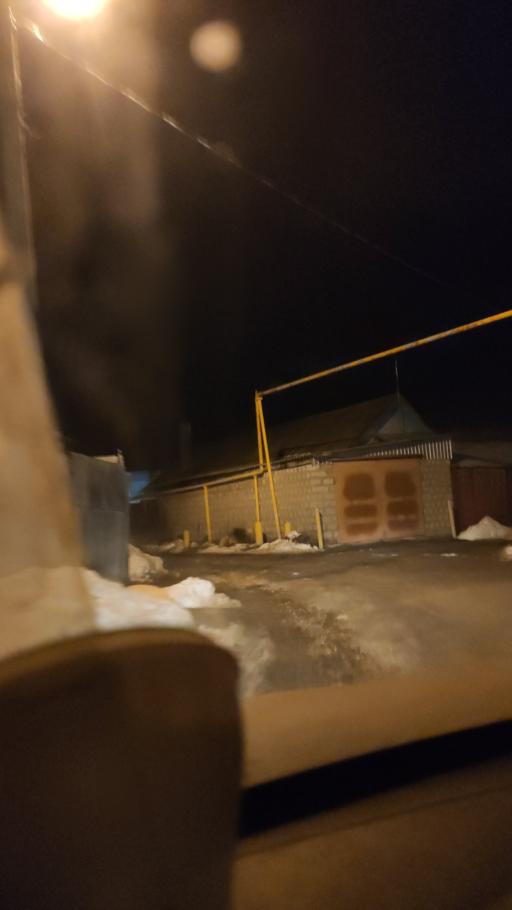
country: RU
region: Samara
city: Samara
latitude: 53.1791
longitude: 50.1540
